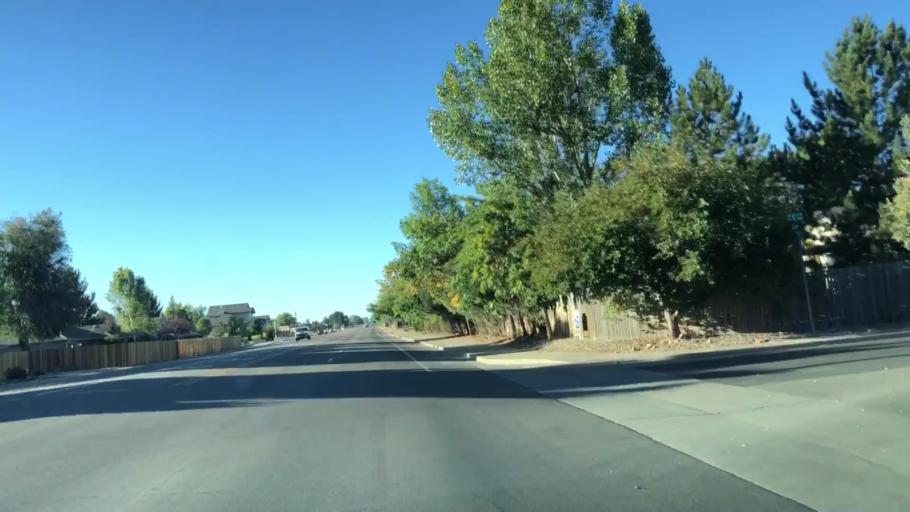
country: US
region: Colorado
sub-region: Larimer County
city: Loveland
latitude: 40.3880
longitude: -105.1161
